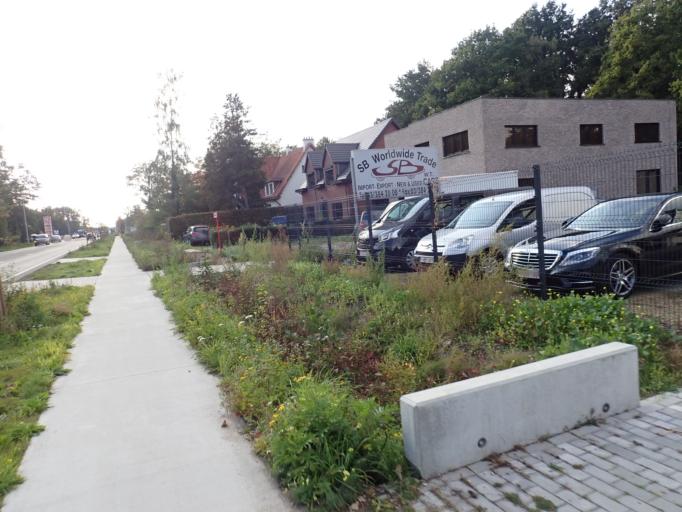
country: BE
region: Flanders
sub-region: Provincie Antwerpen
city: Schilde
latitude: 51.2481
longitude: 4.6013
